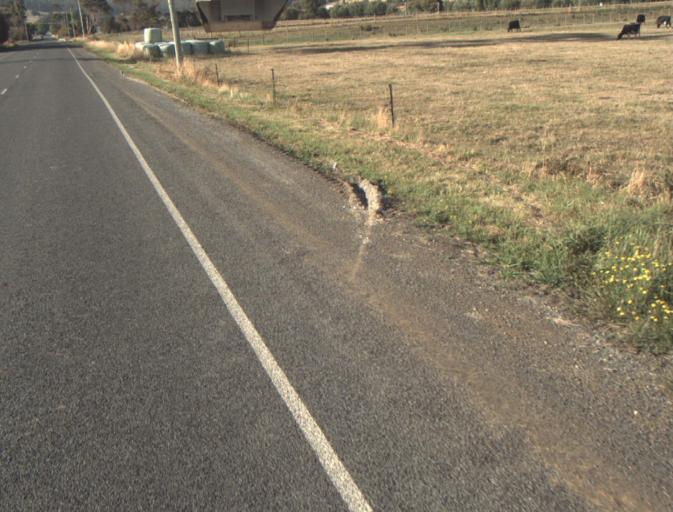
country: AU
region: Tasmania
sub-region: Launceston
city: Mayfield
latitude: -41.2392
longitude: 147.2157
